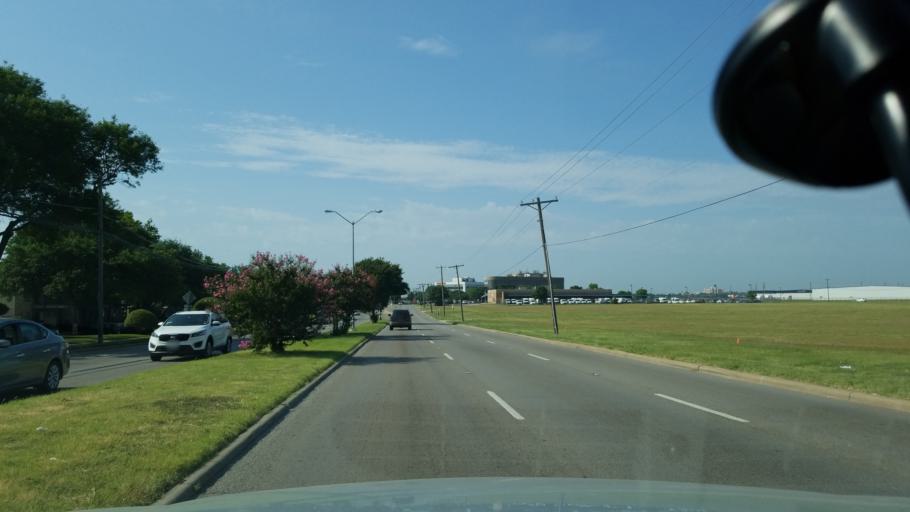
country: US
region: Texas
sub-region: Dallas County
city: Duncanville
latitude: 32.6826
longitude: -96.8571
